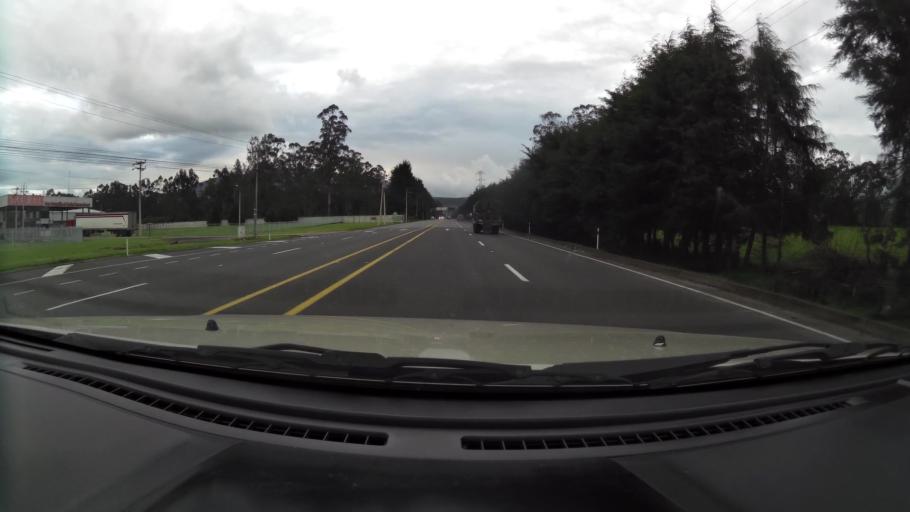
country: EC
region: Pichincha
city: Machachi
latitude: -0.4633
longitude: -78.5712
